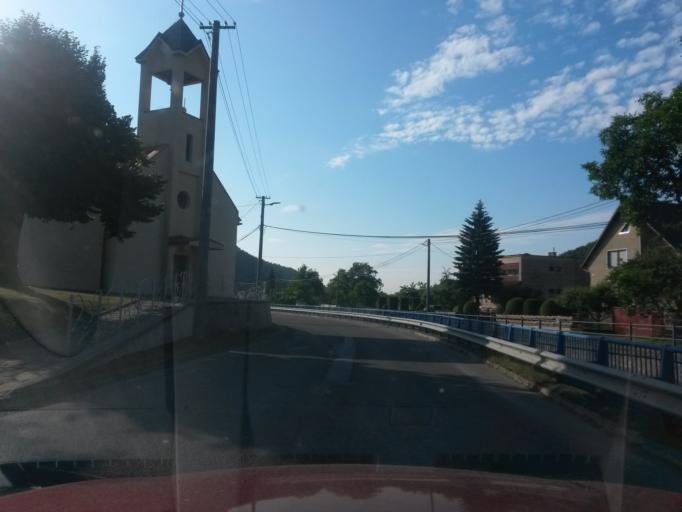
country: SK
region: Presovsky
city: Sabinov
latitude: 49.0865
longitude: 21.0236
